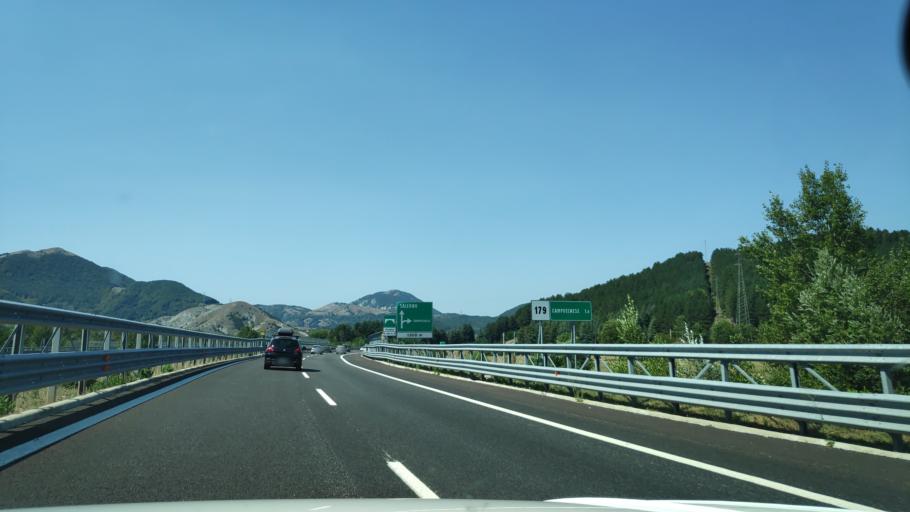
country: IT
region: Calabria
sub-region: Provincia di Cosenza
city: Morano Calabro
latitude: 39.8638
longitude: 16.0900
